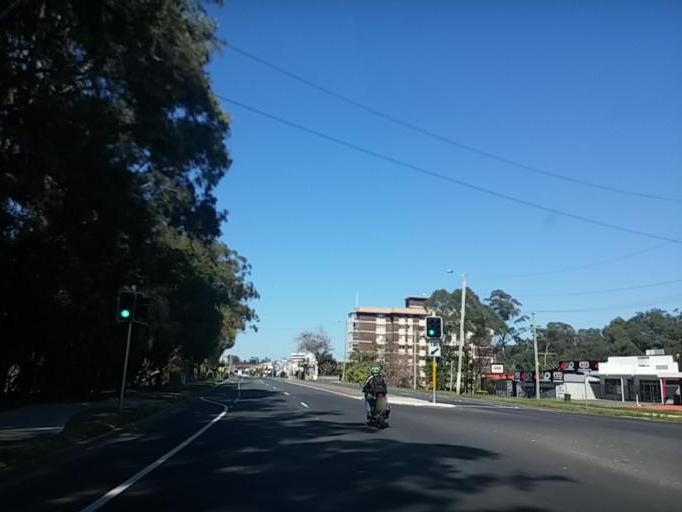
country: AU
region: New South Wales
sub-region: Coffs Harbour
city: Coffs Harbour
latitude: -30.2926
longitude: 153.1175
